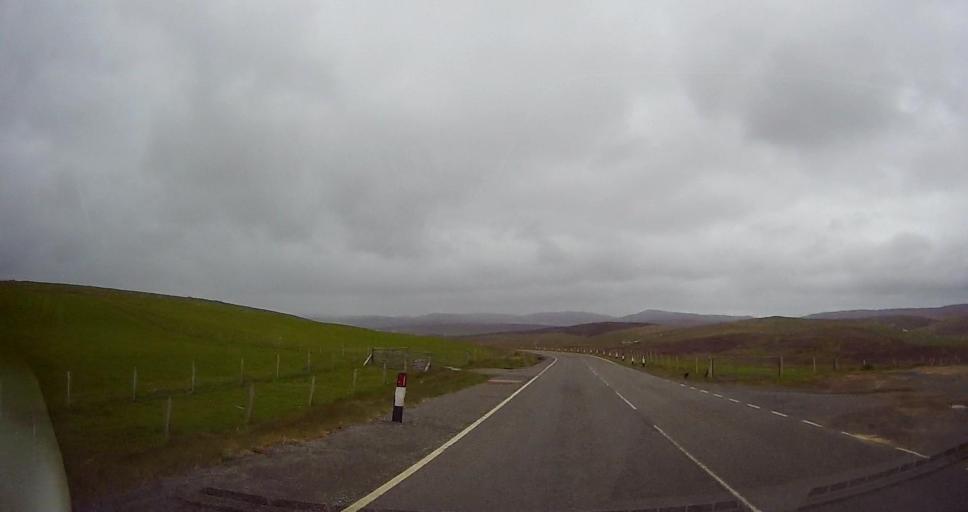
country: GB
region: Scotland
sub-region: Shetland Islands
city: Lerwick
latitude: 60.2633
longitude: -1.4008
